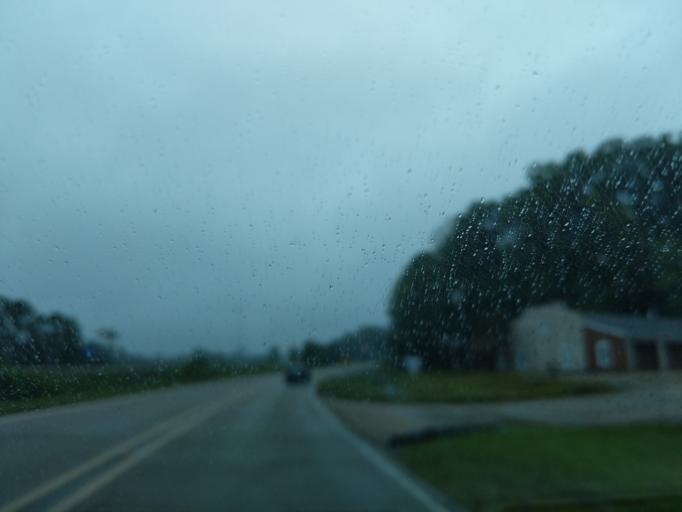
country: US
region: Mississippi
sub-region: Warren County
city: Vicksburg
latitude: 32.3274
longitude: -90.8616
